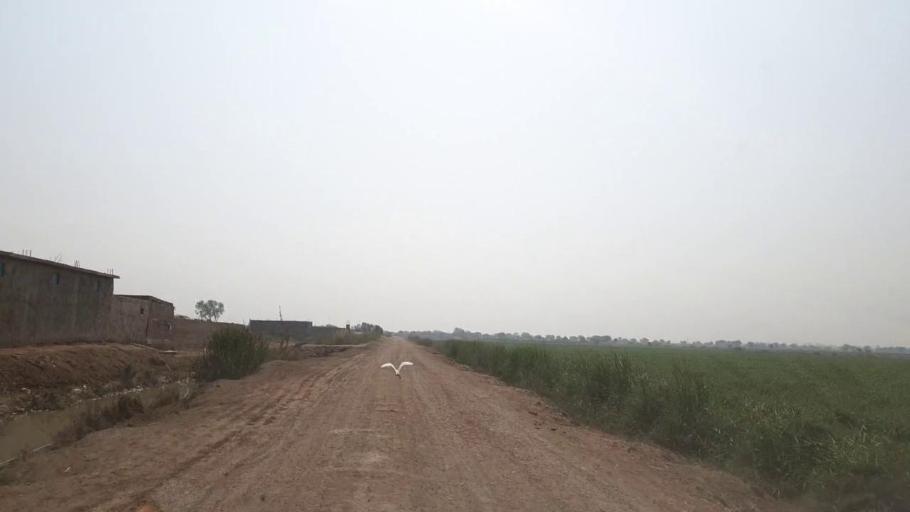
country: PK
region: Sindh
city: Mirpur Khas
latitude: 25.5405
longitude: 69.0616
